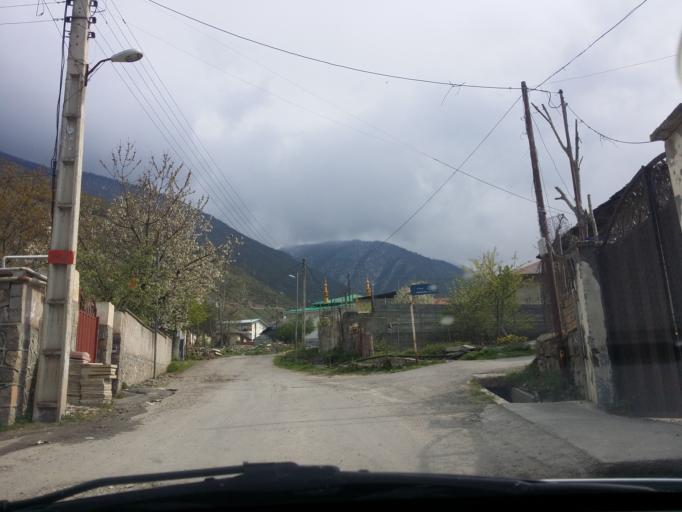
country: IR
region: Mazandaran
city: `Abbasabad
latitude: 36.4837
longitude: 51.1387
